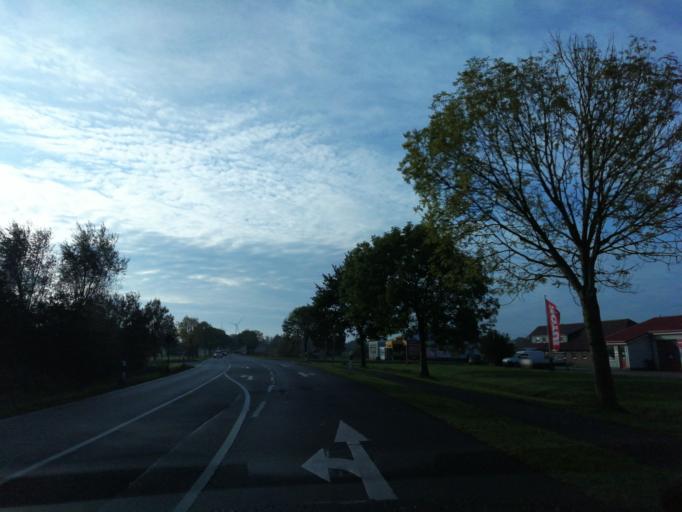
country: DE
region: Lower Saxony
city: Sillenstede
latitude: 53.6320
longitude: 8.0148
